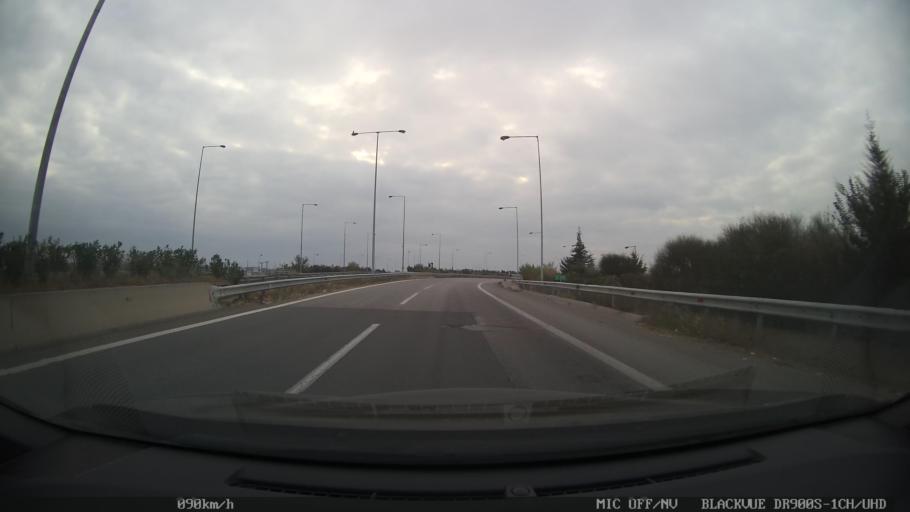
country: GR
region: Central Macedonia
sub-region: Nomos Thessalonikis
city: Kalochori
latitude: 40.6563
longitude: 22.8414
